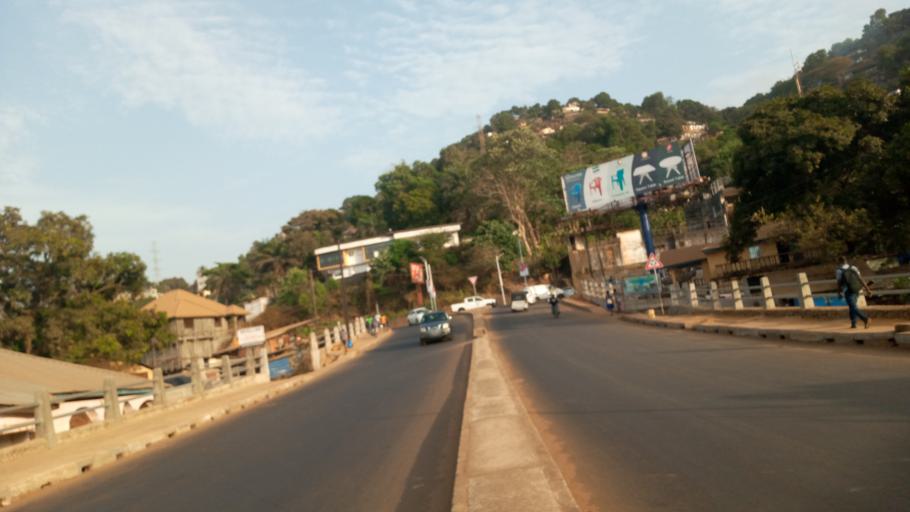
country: SL
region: Western Area
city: Freetown
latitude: 8.4698
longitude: -13.2459
